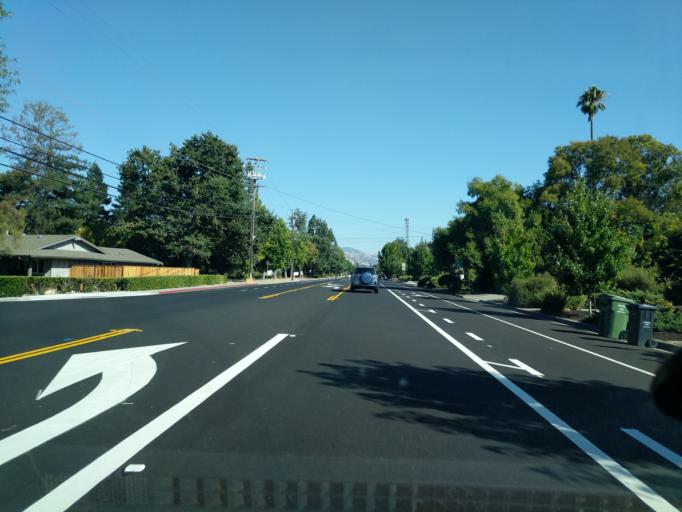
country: US
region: California
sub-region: Contra Costa County
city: Waldon
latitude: 37.9198
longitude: -122.0326
